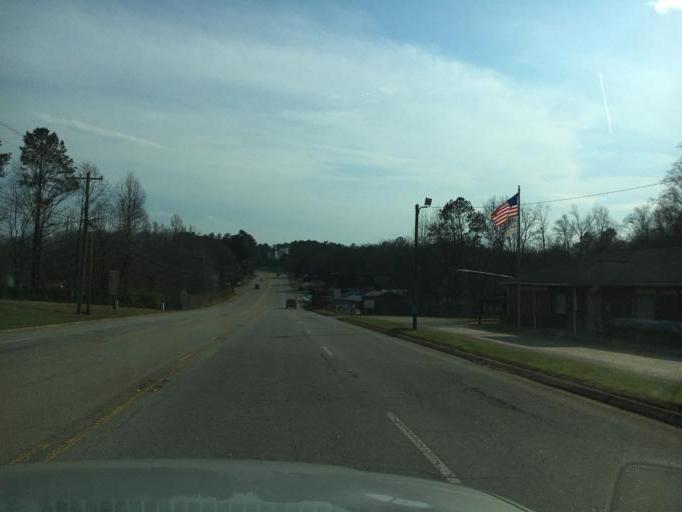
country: US
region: South Carolina
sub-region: Spartanburg County
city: Mayo
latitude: 35.1316
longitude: -81.8636
